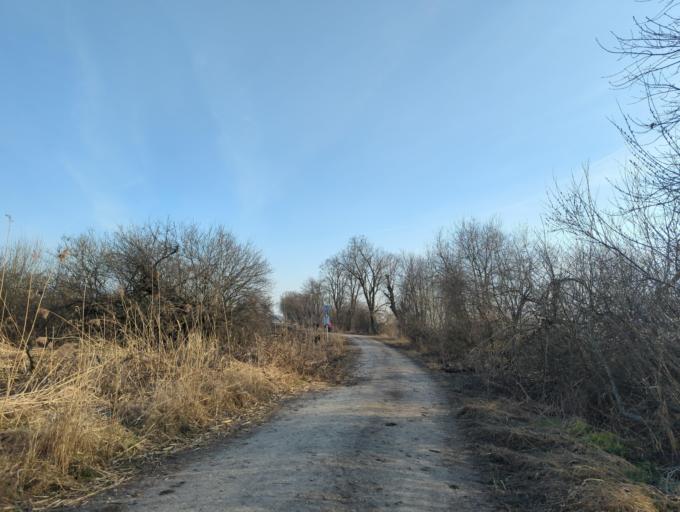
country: DE
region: Bavaria
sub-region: Swabia
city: Leipheim
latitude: 48.4749
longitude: 10.2021
